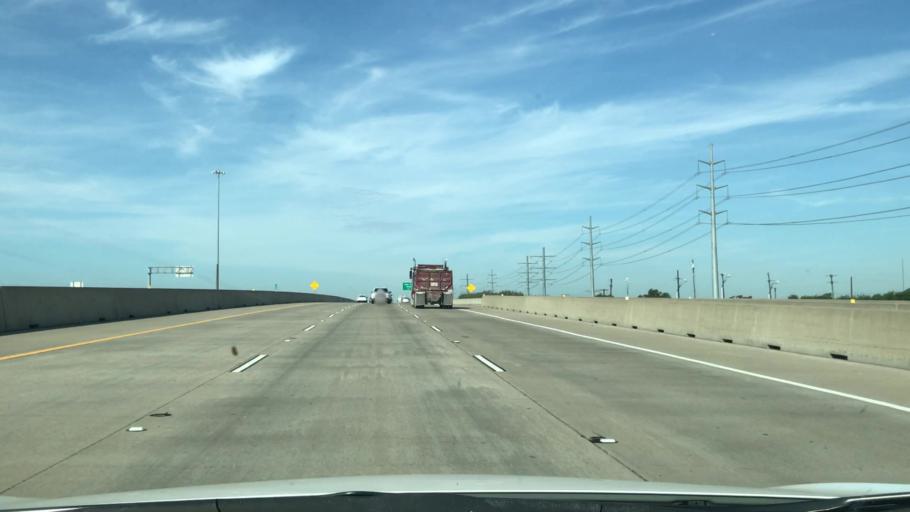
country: US
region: Texas
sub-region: Collin County
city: Fairview
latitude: 33.1517
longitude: -96.6613
